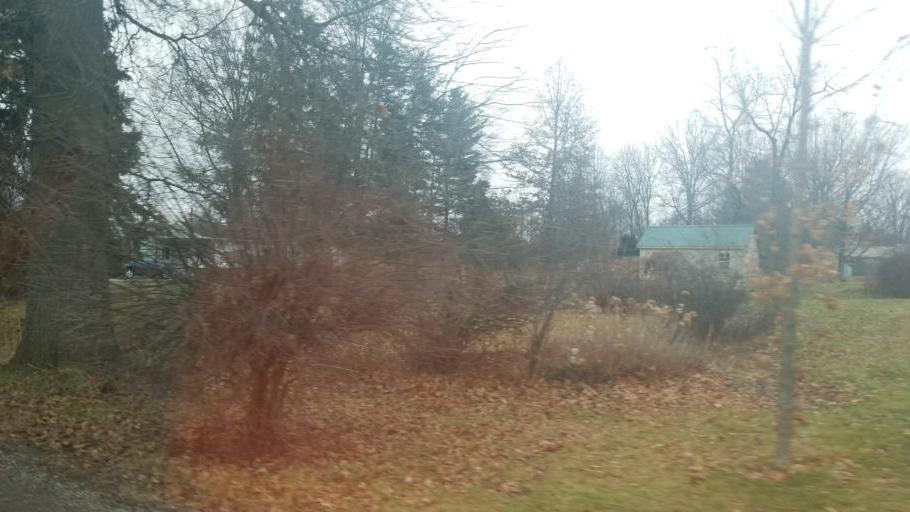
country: US
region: Ohio
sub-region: Crawford County
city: Galion
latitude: 40.7224
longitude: -82.7991
